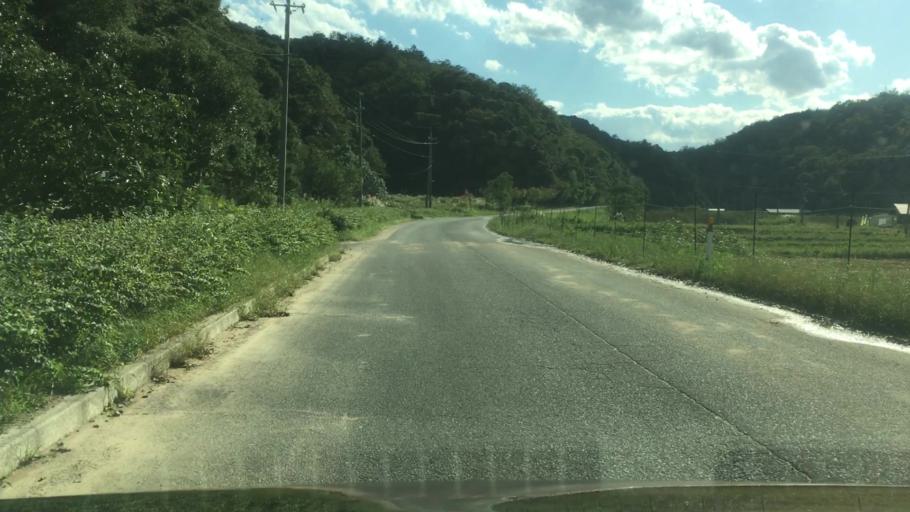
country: JP
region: Hyogo
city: Toyooka
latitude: 35.6473
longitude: 134.9645
